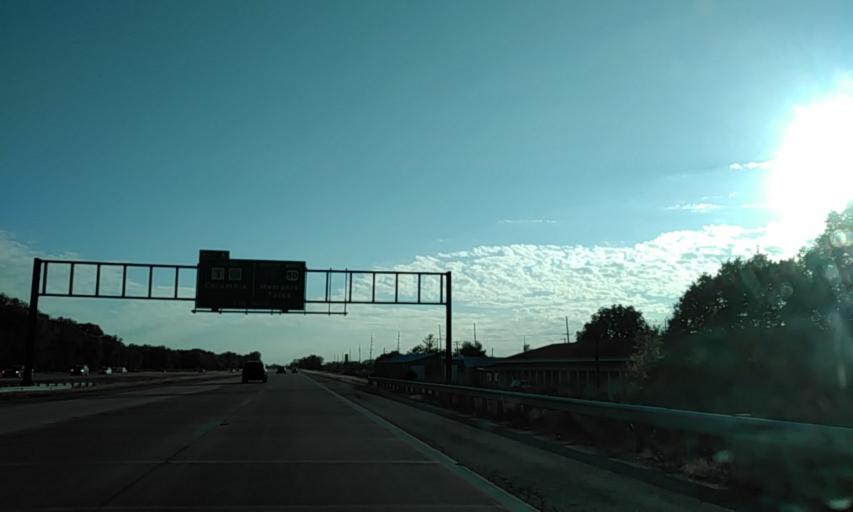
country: US
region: Illinois
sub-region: Saint Clair County
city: Dupo
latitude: 38.5028
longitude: -90.2095
